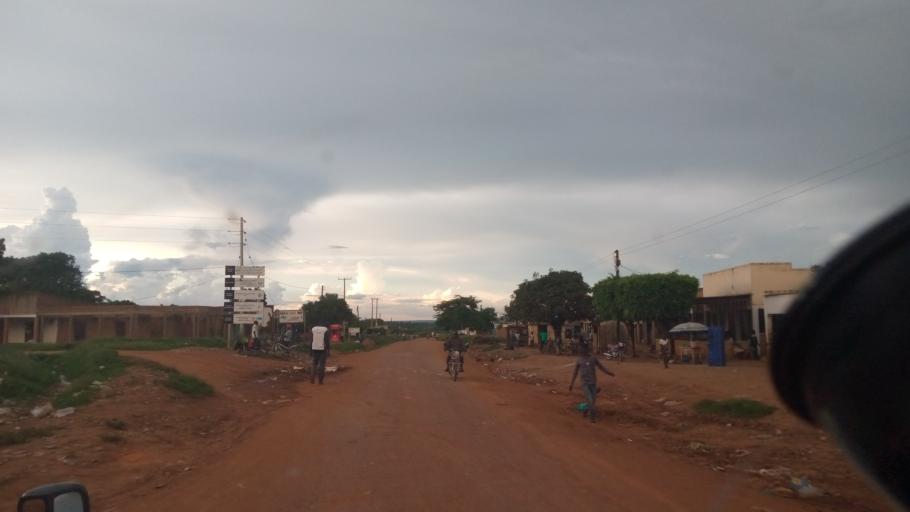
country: UG
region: Northern Region
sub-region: Kole District
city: Kole
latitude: 2.4877
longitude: 32.9351
